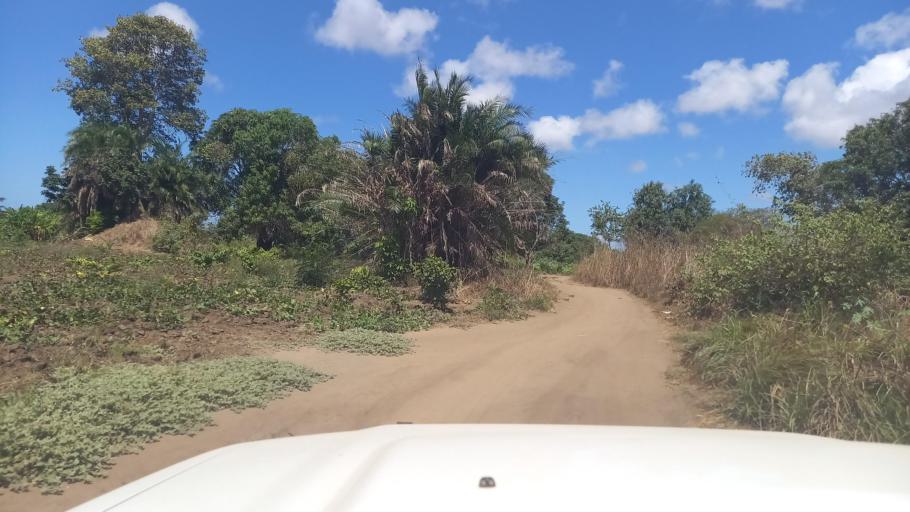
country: MZ
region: Cabo Delgado
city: Pemba
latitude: -13.4244
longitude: 40.4835
